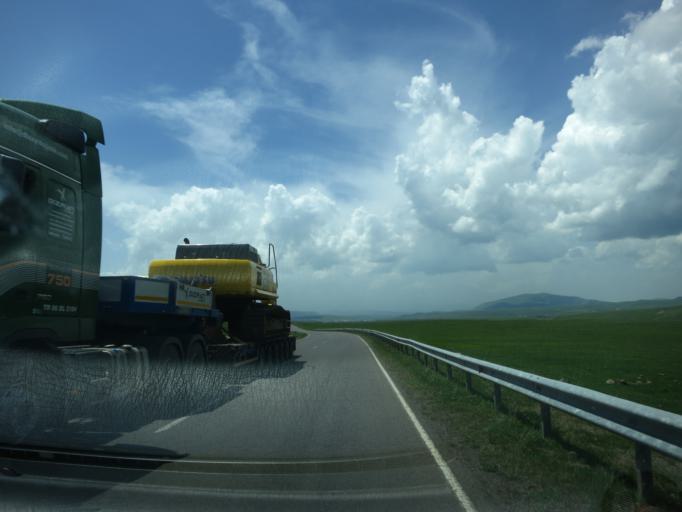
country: GE
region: Samtskhe-Javakheti
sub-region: Ninotsminda
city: Ninotsminda
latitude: 41.2921
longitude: 43.7108
